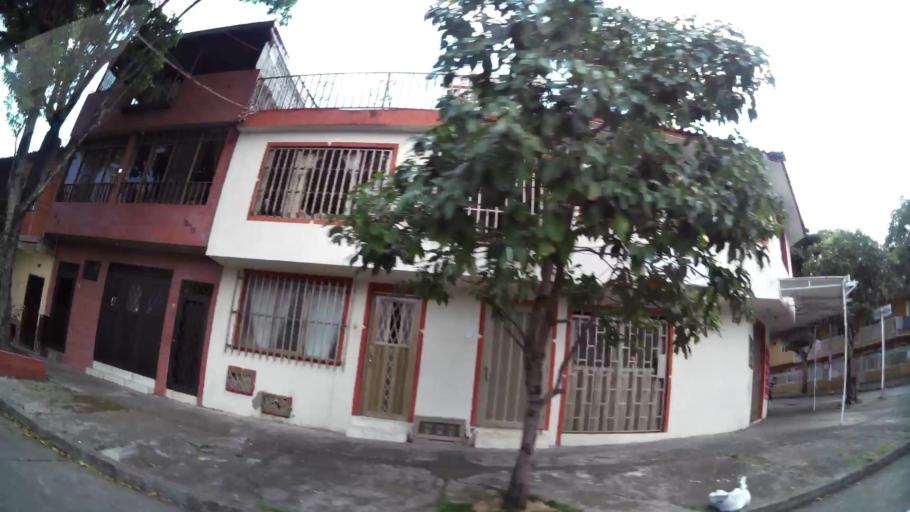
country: CO
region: Valle del Cauca
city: Cali
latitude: 3.4381
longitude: -76.5244
